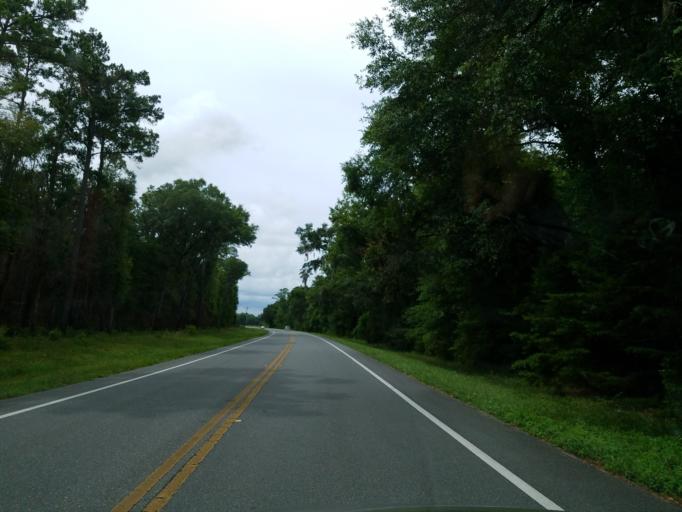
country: US
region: Florida
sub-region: Alachua County
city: High Springs
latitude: 29.8842
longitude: -82.4917
